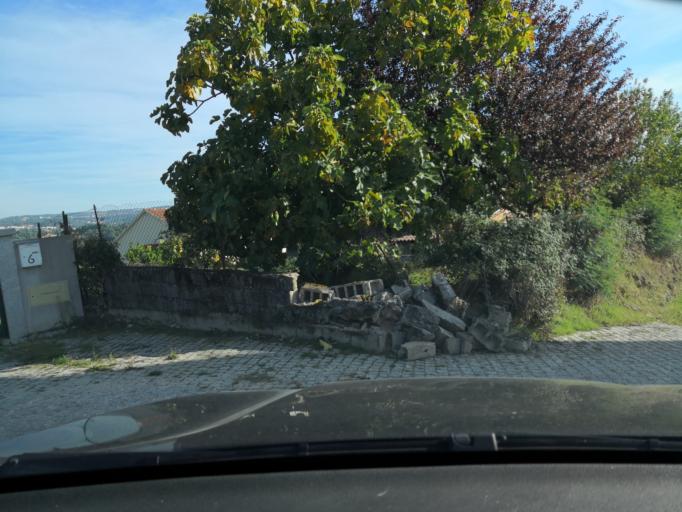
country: PT
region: Vila Real
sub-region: Vila Real
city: Vila Real
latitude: 41.3310
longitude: -7.7415
